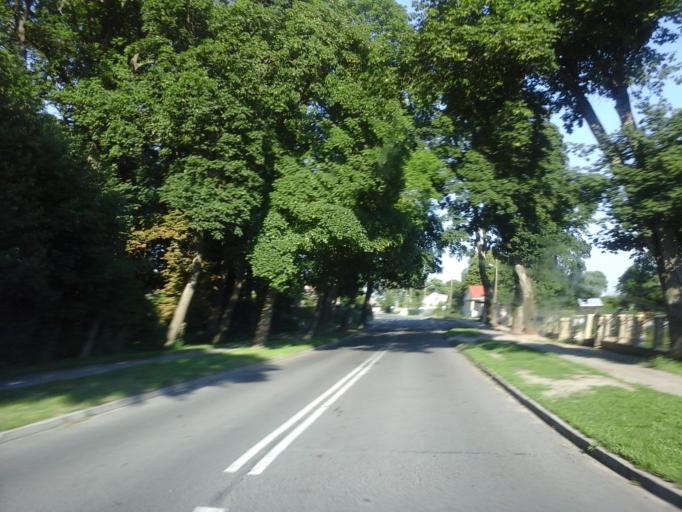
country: PL
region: West Pomeranian Voivodeship
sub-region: Powiat stargardzki
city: Chociwel
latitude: 53.4381
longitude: 15.3579
